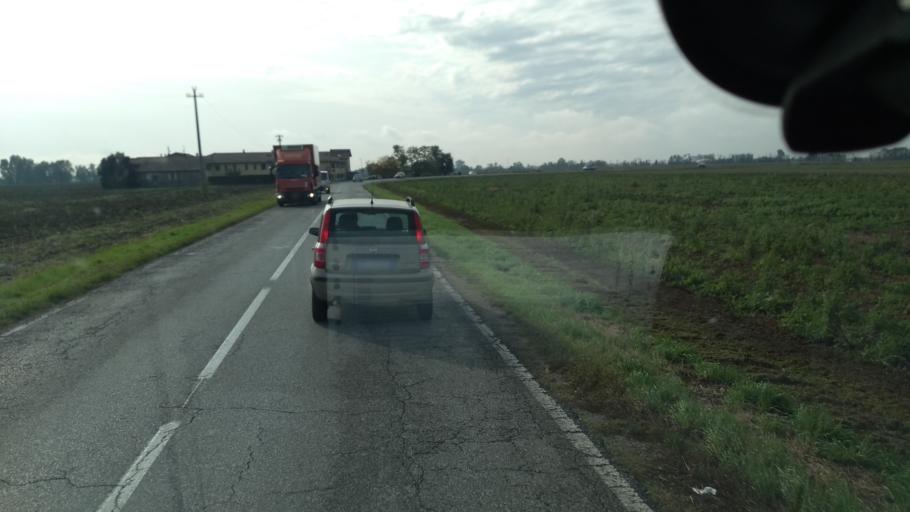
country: IT
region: Lombardy
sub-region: Provincia di Bergamo
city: Cologno al Serio
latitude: 45.5647
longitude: 9.6932
